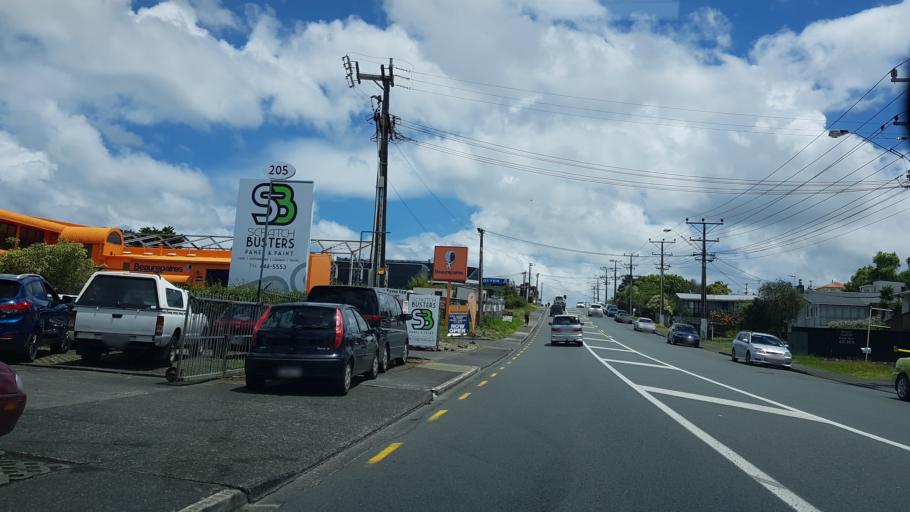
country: NZ
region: Auckland
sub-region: Auckland
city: North Shore
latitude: -36.7807
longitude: 174.7396
